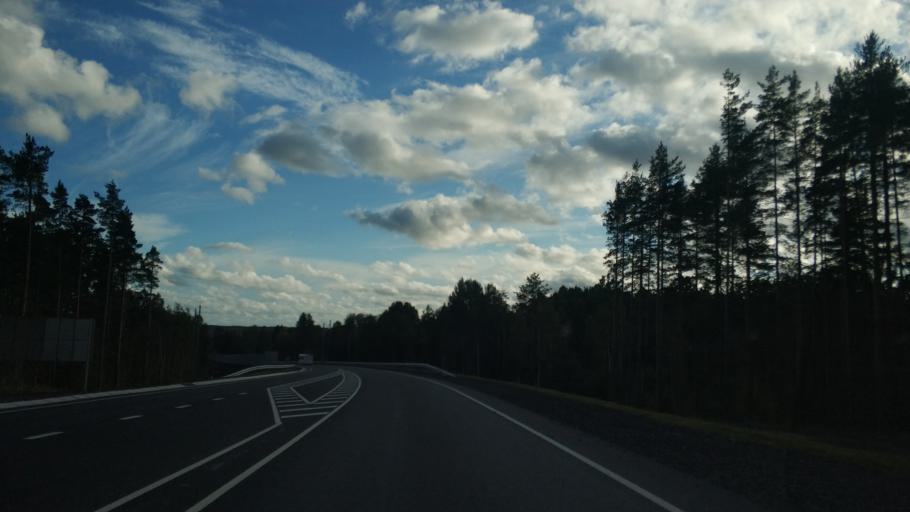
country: RU
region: Leningrad
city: Priozersk
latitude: 60.8403
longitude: 30.1249
